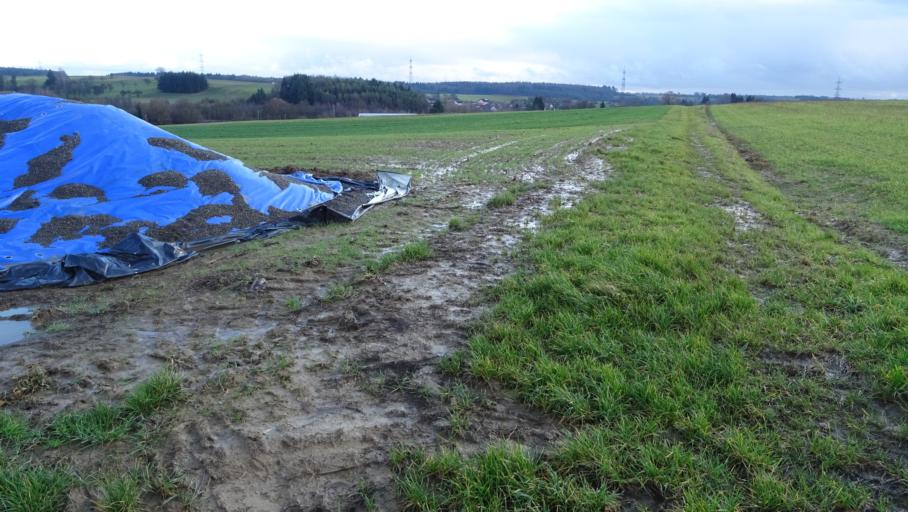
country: DE
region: Baden-Wuerttemberg
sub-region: Karlsruhe Region
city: Seckach
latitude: 49.4372
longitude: 9.2878
